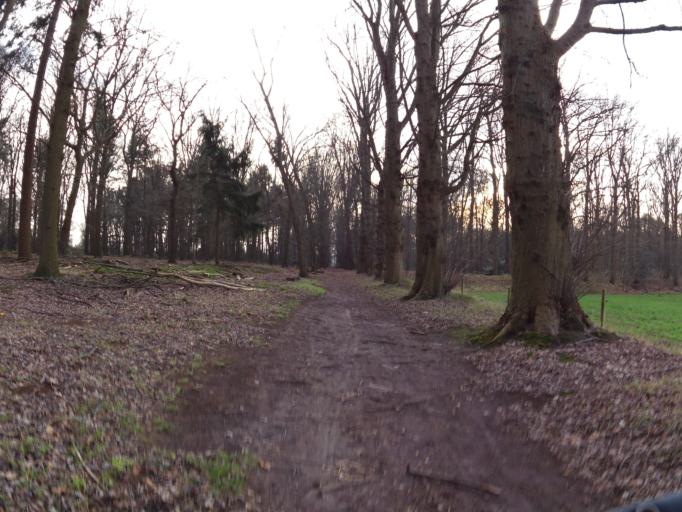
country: NL
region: North Brabant
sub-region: Gemeente 's-Hertogenbosch
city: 's-Hertogenbosch
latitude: 51.6684
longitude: 5.3217
